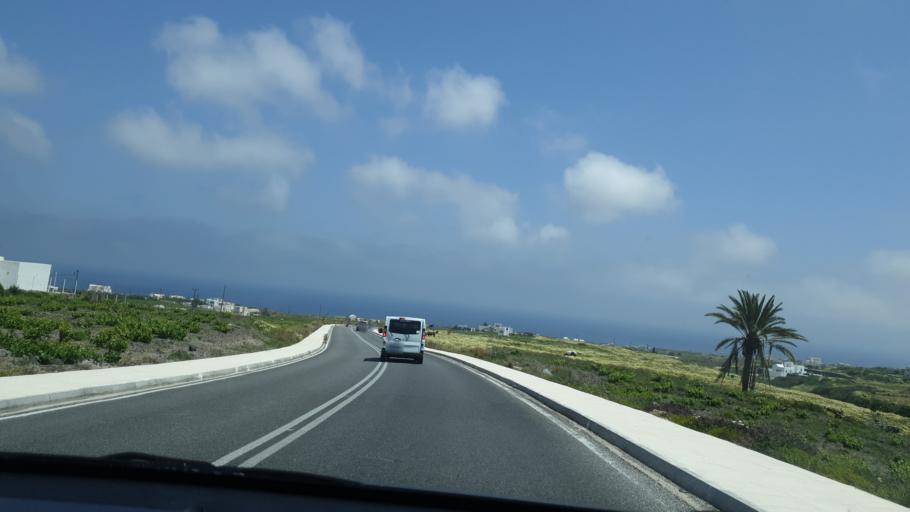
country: GR
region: South Aegean
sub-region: Nomos Kykladon
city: Fira
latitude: 36.4172
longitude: 25.4463
